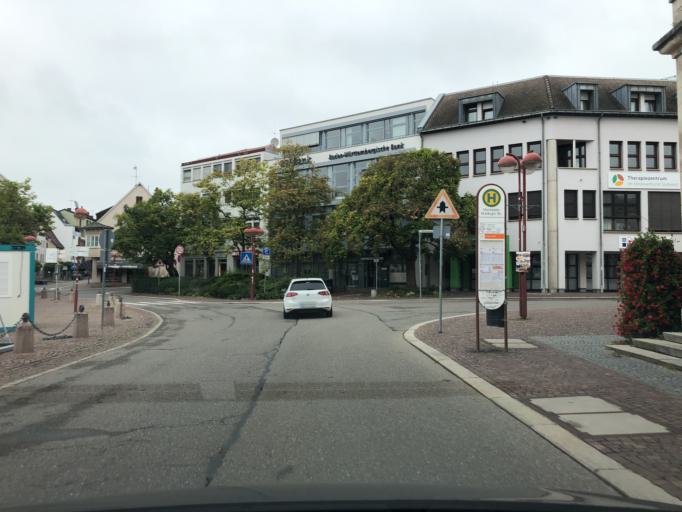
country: DE
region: Baden-Wuerttemberg
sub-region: Regierungsbezirk Stuttgart
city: Sindelfingen
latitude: 48.7080
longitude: 9.0039
